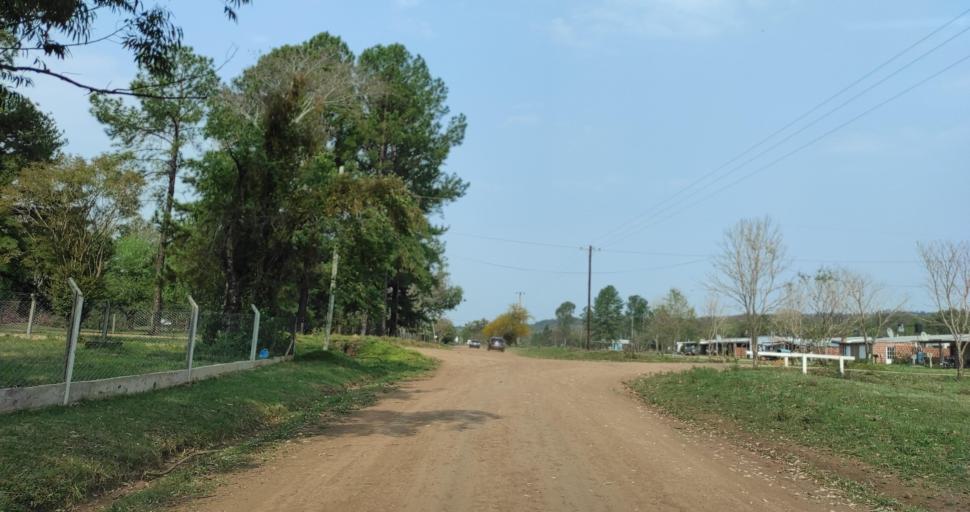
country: AR
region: Misiones
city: Cerro Cora
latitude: -27.5135
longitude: -55.6046
